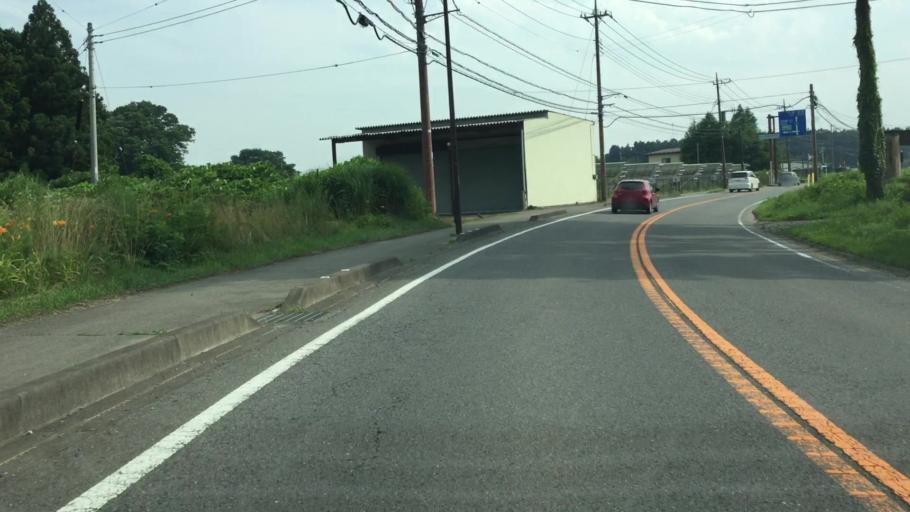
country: JP
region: Tochigi
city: Kuroiso
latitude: 36.9943
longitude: 139.9426
